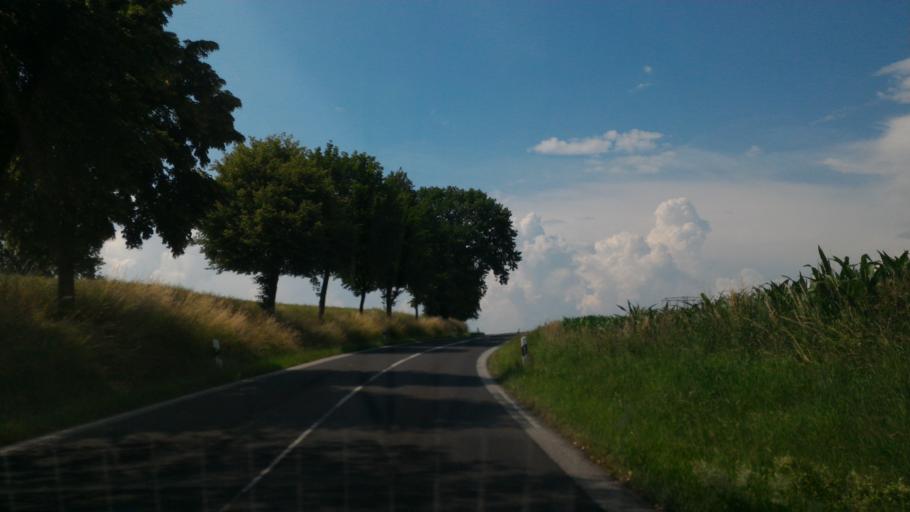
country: DE
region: Saxony
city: Hirschfelde
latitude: 50.9270
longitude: 14.8630
